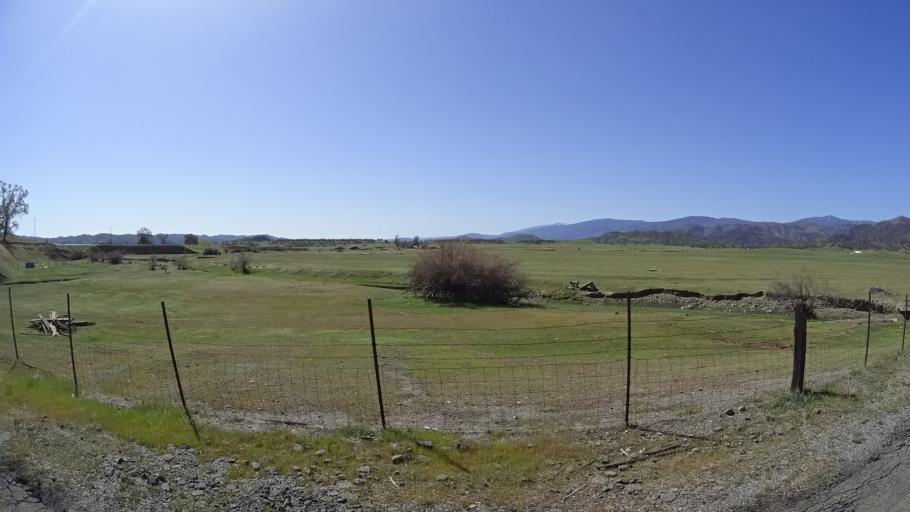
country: US
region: California
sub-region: Tehama County
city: Rancho Tehama Reserve
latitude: 39.6995
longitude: -122.5518
